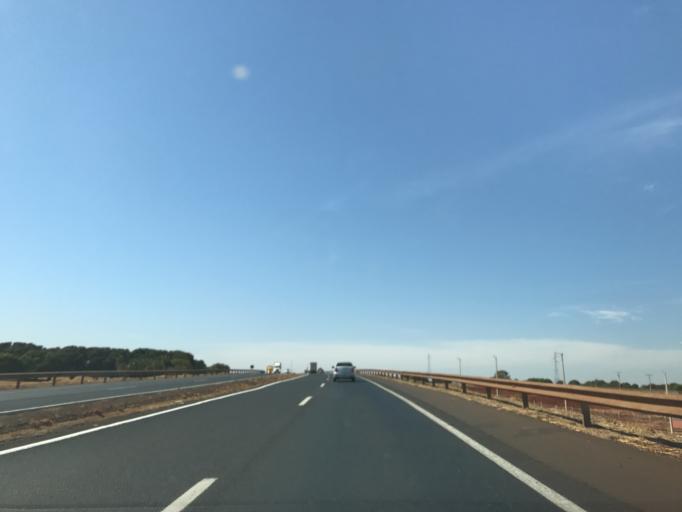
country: BR
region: Minas Gerais
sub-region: Centralina
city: Centralina
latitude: -18.7089
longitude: -49.1392
